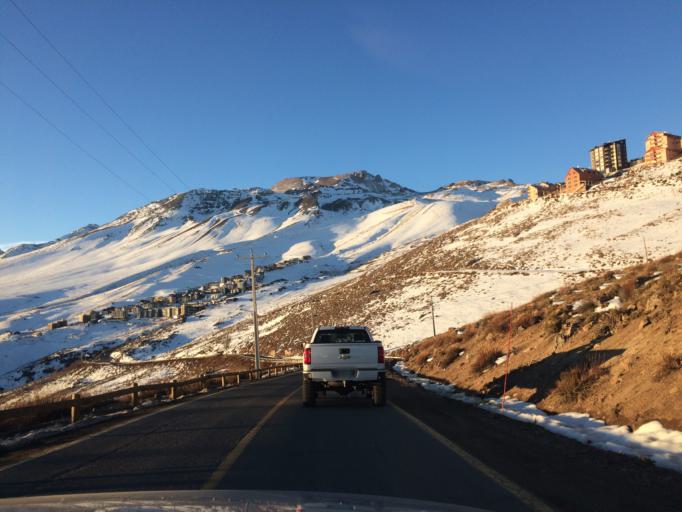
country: CL
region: Santiago Metropolitan
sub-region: Provincia de Santiago
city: Villa Presidente Frei, Nunoa, Santiago, Chile
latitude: -33.3479
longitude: -70.2959
